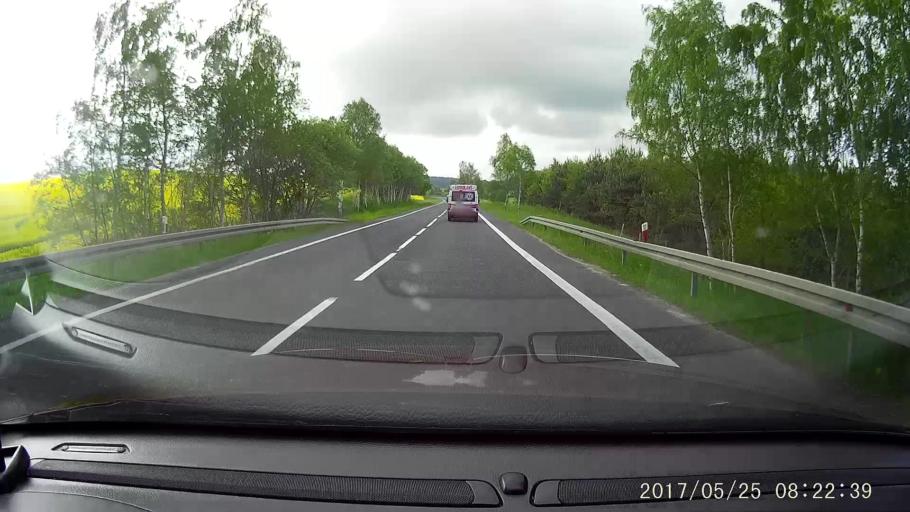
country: PL
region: Lower Silesian Voivodeship
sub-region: Powiat jeleniogorski
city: Stara Kamienica
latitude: 50.9278
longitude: 15.6069
